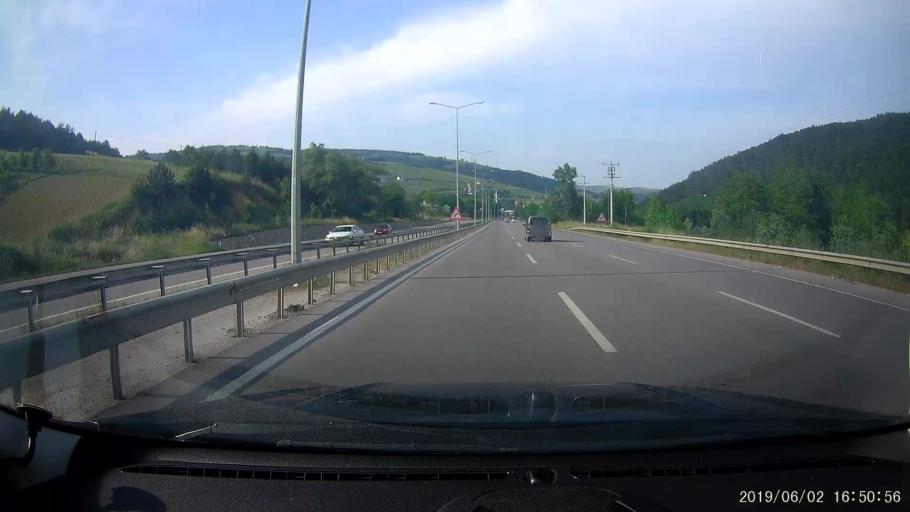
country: TR
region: Samsun
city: Taflan
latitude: 41.2651
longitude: 36.1766
